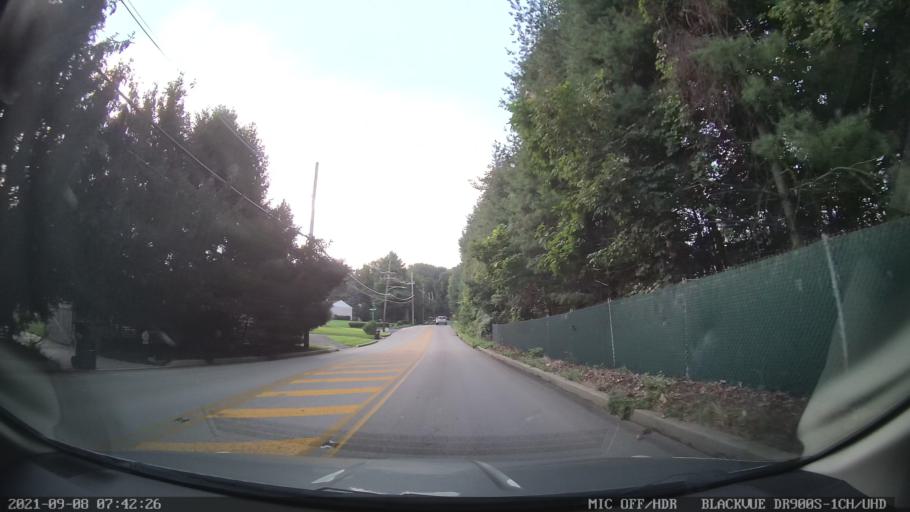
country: US
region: Pennsylvania
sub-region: Montgomery County
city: King of Prussia
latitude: 40.0763
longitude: -75.3826
